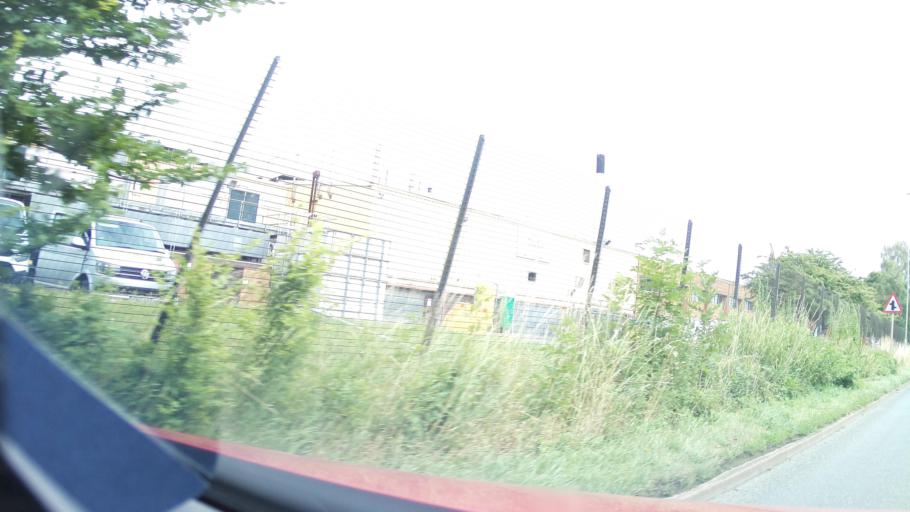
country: GB
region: England
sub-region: Northamptonshire
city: Corby
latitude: 52.5116
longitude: -0.6962
